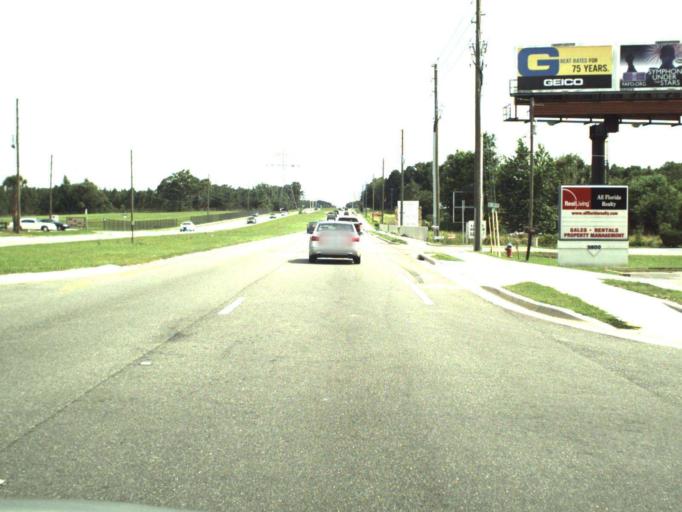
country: US
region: Florida
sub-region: Marion County
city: Silver Springs Shores
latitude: 29.1513
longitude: -82.0538
